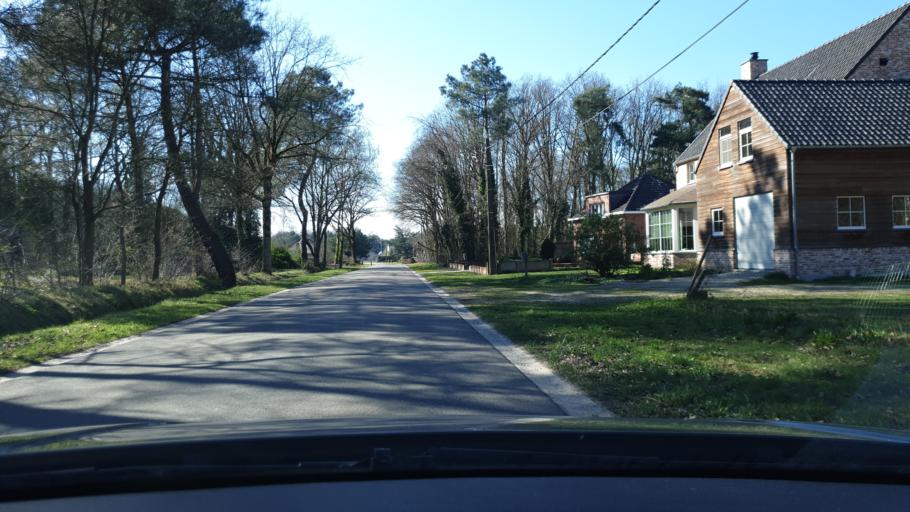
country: BE
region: Flanders
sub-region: Provincie Antwerpen
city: Geel
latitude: 51.1338
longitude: 5.0163
